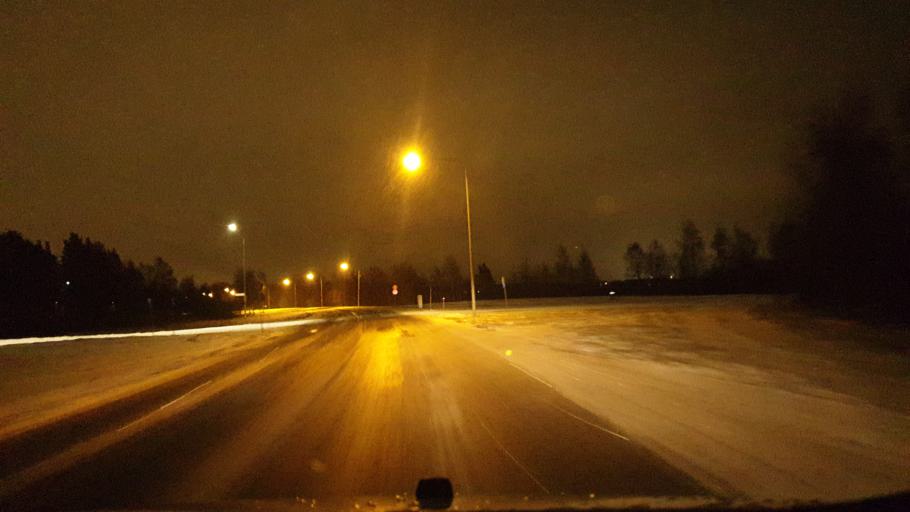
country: FI
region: Northern Ostrobothnia
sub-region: Oulu
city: Oulu
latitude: 64.9834
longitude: 25.4485
